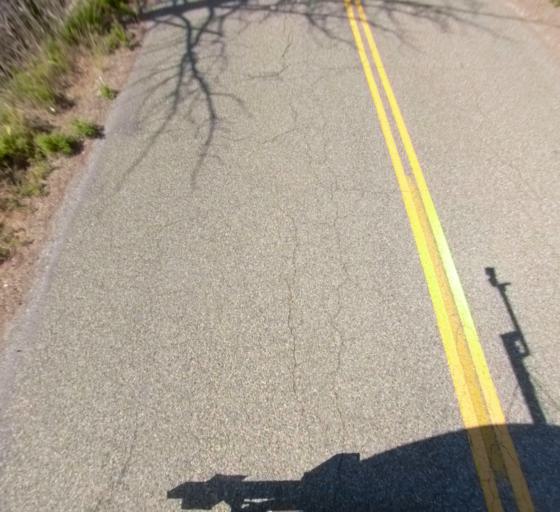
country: US
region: California
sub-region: Fresno County
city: Auberry
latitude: 37.2488
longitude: -119.3470
